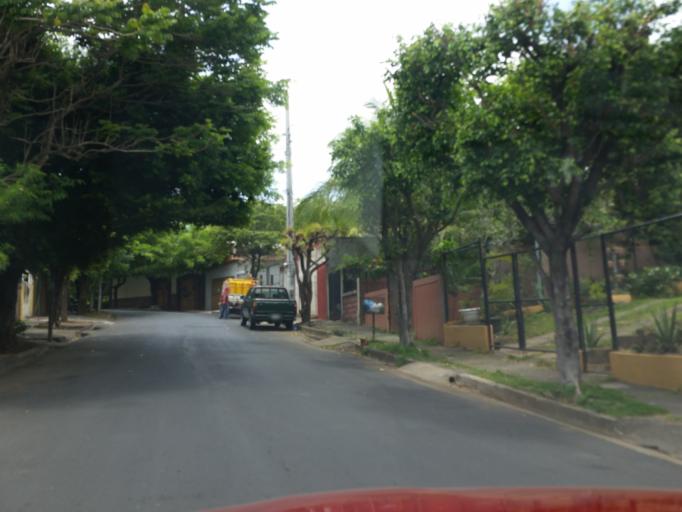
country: NI
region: Managua
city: Managua
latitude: 12.1010
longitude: -86.2755
